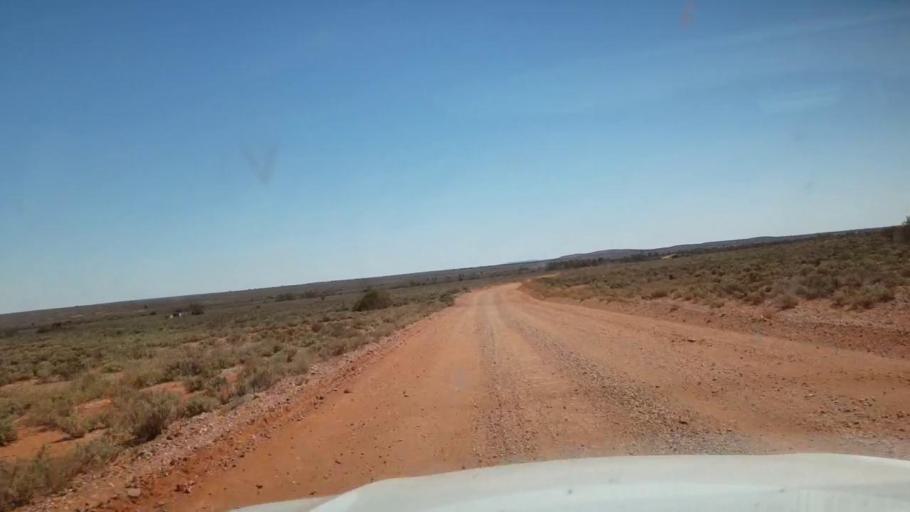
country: AU
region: South Australia
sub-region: Whyalla
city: Whyalla
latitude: -32.6858
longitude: 137.1174
